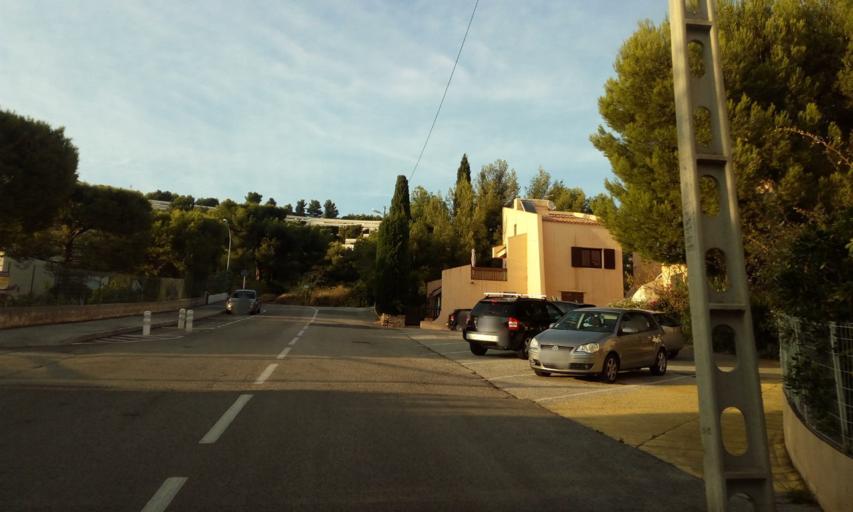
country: FR
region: Provence-Alpes-Cote d'Azur
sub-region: Departement du Var
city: Bandol
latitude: 43.1422
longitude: 5.7583
